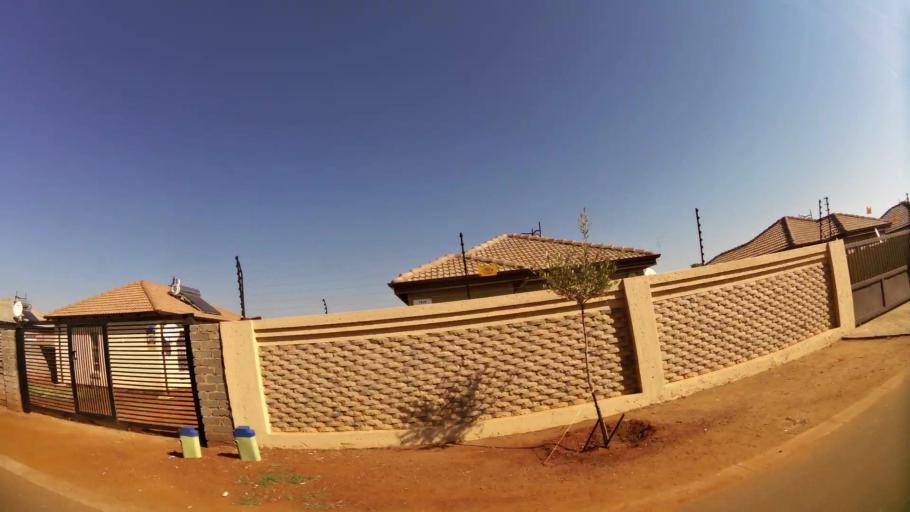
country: ZA
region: North-West
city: Ga-Rankuwa
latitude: -25.6360
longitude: 28.0737
